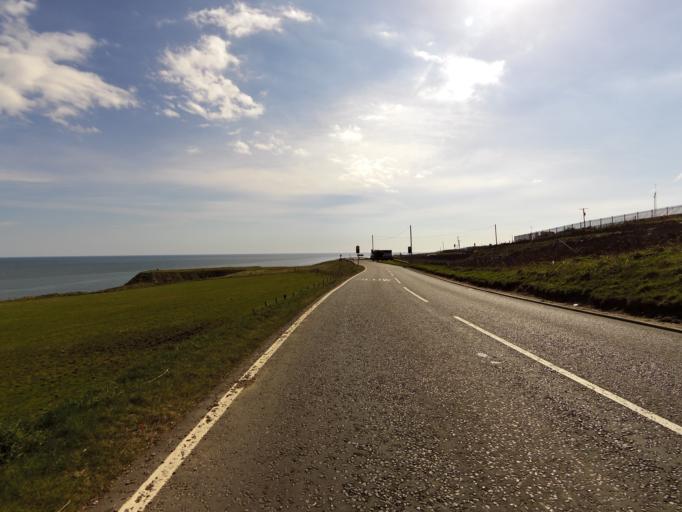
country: GB
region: Scotland
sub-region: Aberdeen City
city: Aberdeen
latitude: 57.1263
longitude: -2.0540
